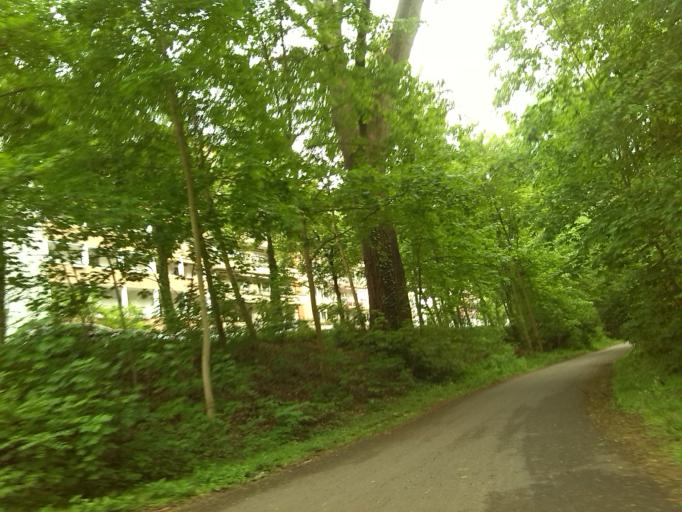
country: DE
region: Rheinland-Pfalz
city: Ludwigshafen am Rhein
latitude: 49.4695
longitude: 8.4666
